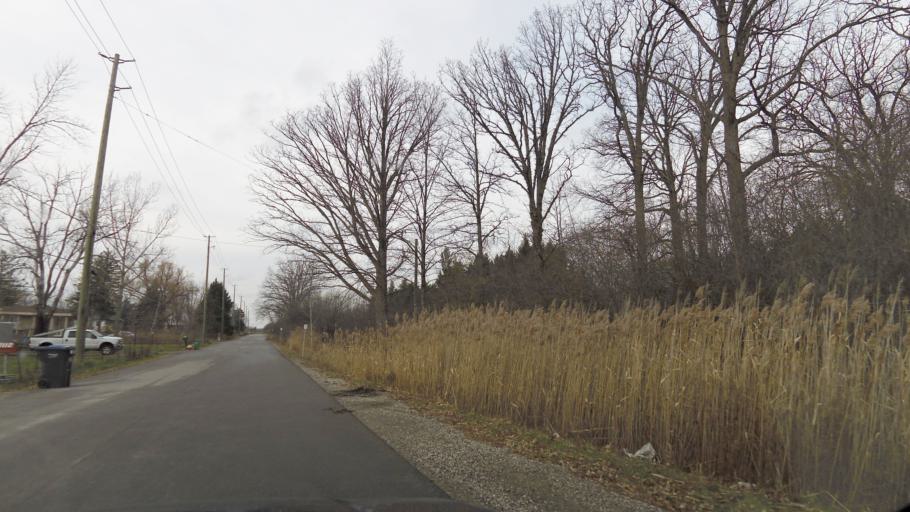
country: CA
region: Ontario
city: Etobicoke
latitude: 43.7448
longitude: -79.6500
